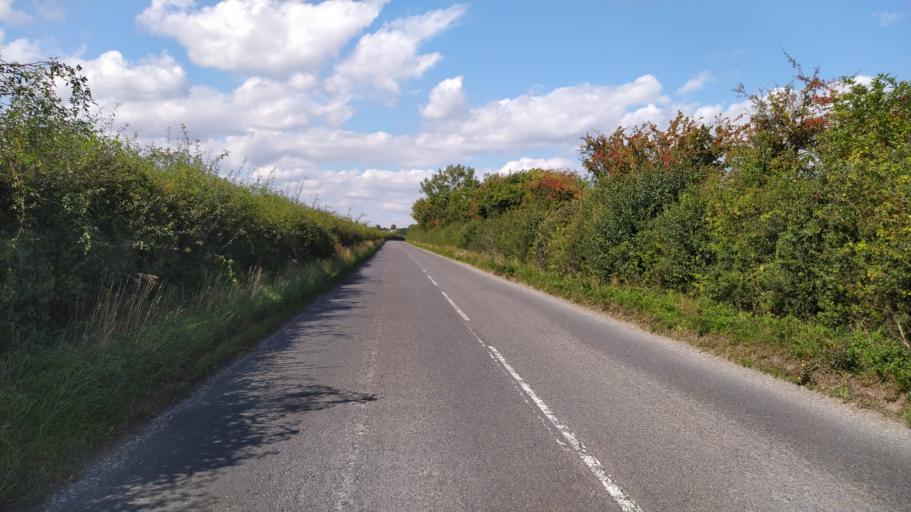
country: GB
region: England
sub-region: Hampshire
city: Abbotts Ann
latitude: 51.1665
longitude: -1.6074
